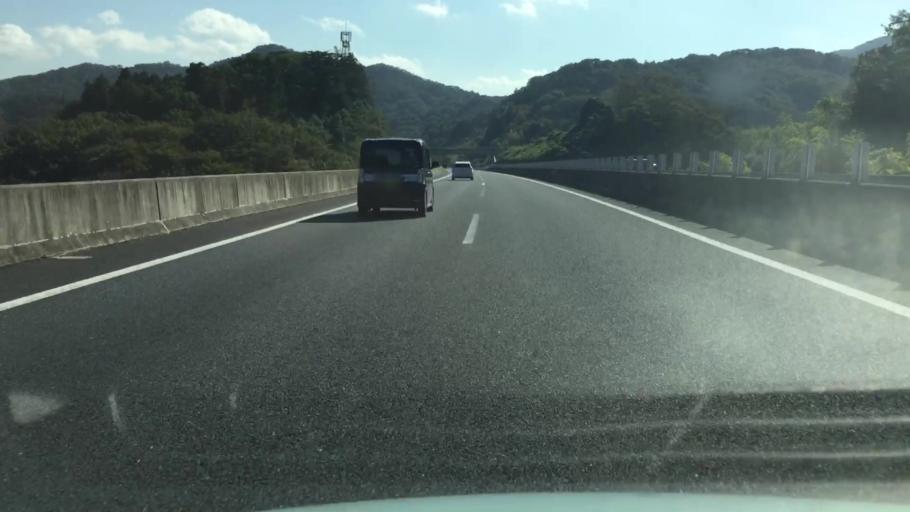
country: JP
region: Ibaraki
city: Kasama
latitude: 36.3416
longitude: 140.2221
